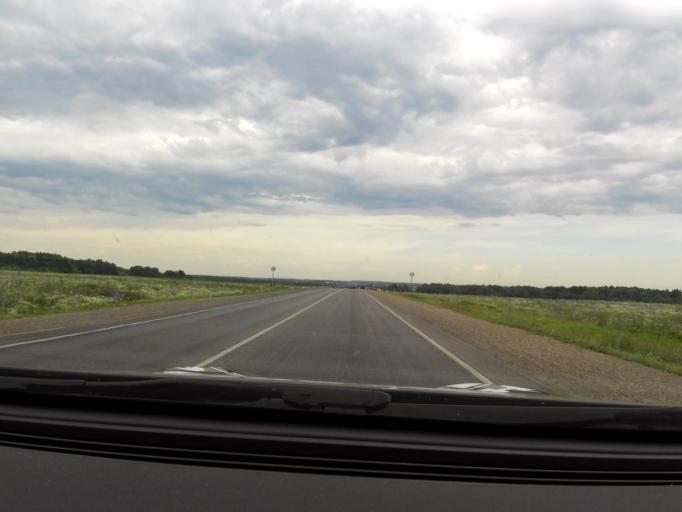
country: RU
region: Bashkortostan
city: Urman
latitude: 54.8173
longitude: 56.8195
